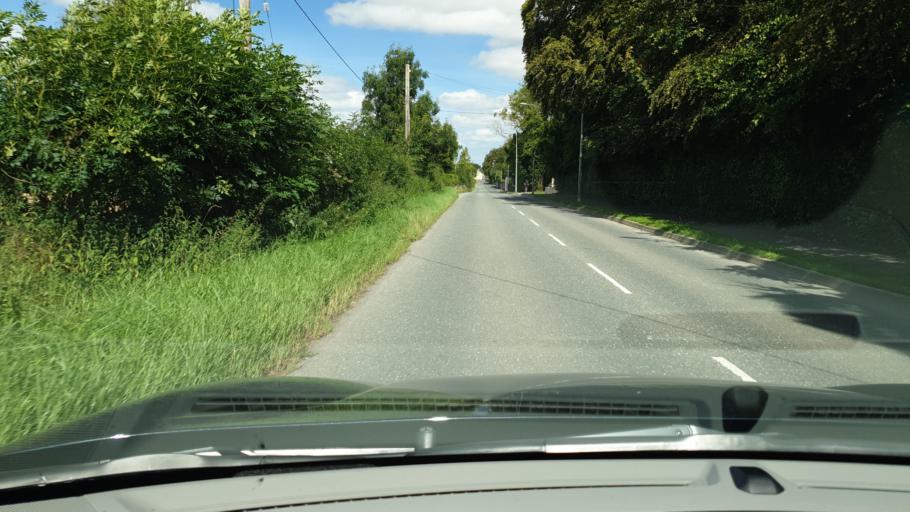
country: IE
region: Leinster
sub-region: An Mhi
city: Dunboyne
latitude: 53.4154
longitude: -6.4828
